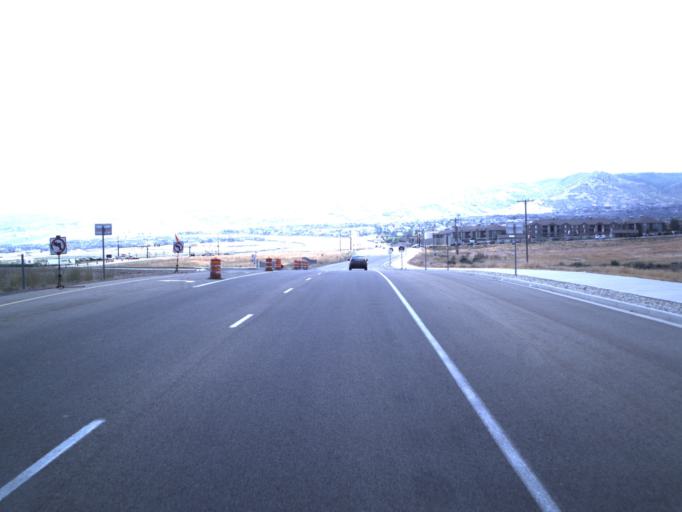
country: US
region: Utah
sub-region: Salt Lake County
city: Herriman
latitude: 40.5123
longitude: -112.0051
